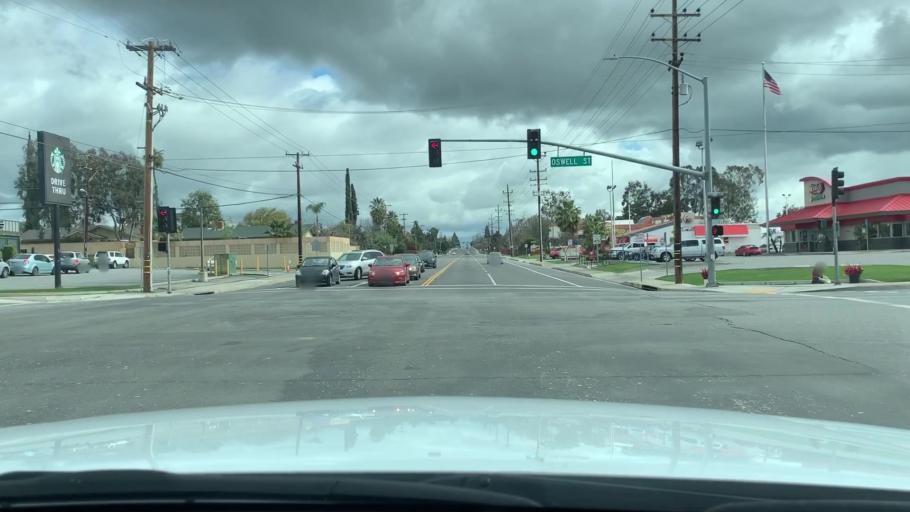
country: US
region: California
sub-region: Kern County
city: Bakersfield
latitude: 35.3977
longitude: -118.9500
